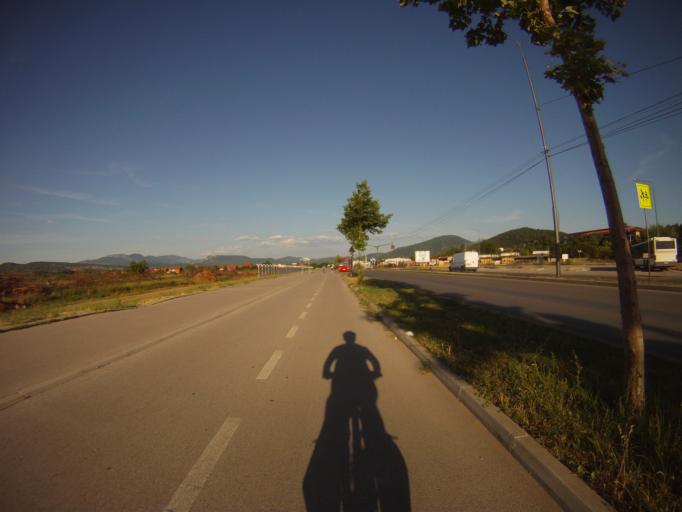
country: RS
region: Central Serbia
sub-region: Nisavski Okrug
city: Nis
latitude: 43.3078
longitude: 21.9509
